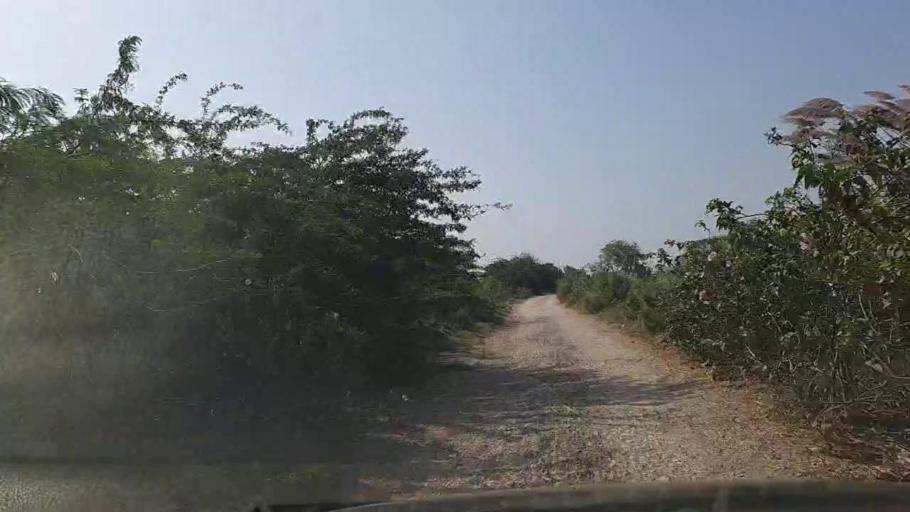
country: PK
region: Sindh
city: Gharo
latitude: 24.6933
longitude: 67.6146
